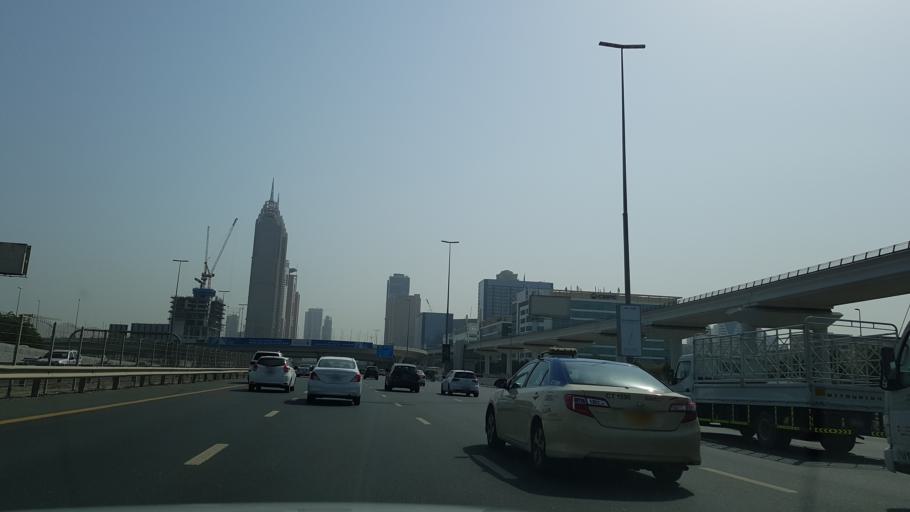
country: AE
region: Dubai
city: Dubai
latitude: 25.0930
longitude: 55.1624
